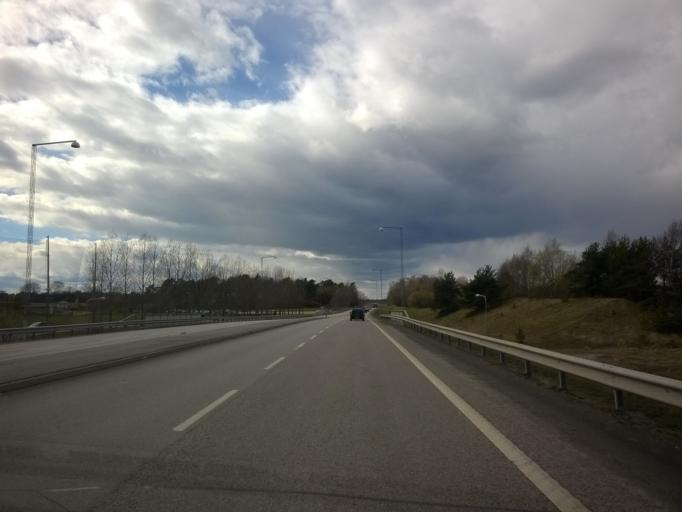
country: SE
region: Stockholm
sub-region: Upplands Vasby Kommun
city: Upplands Vaesby
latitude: 59.4709
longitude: 17.9076
